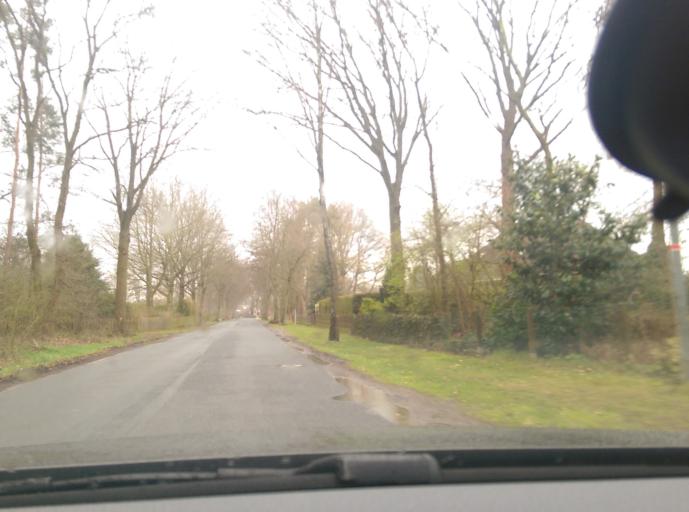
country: DE
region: Lower Saxony
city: Schwarmstedt
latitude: 52.6291
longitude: 9.6042
